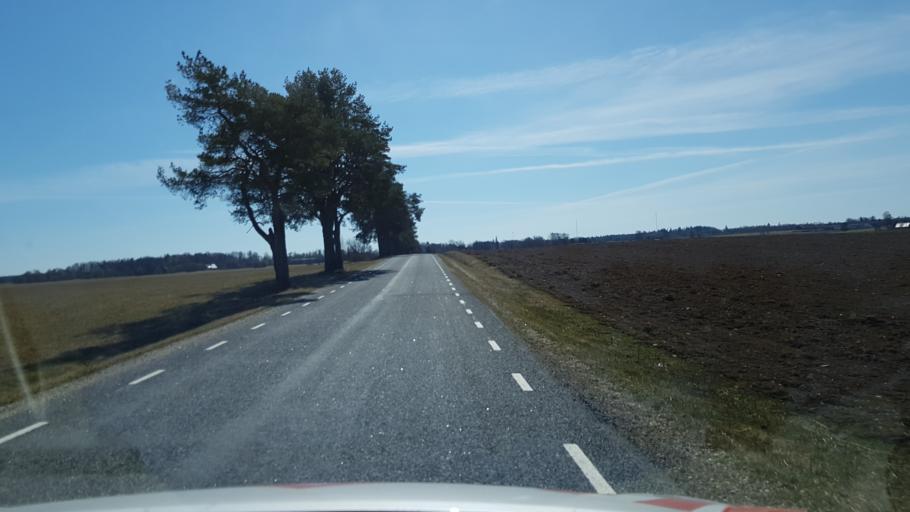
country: EE
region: Laeaene-Virumaa
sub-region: Vinni vald
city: Vinni
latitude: 59.1092
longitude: 26.5248
